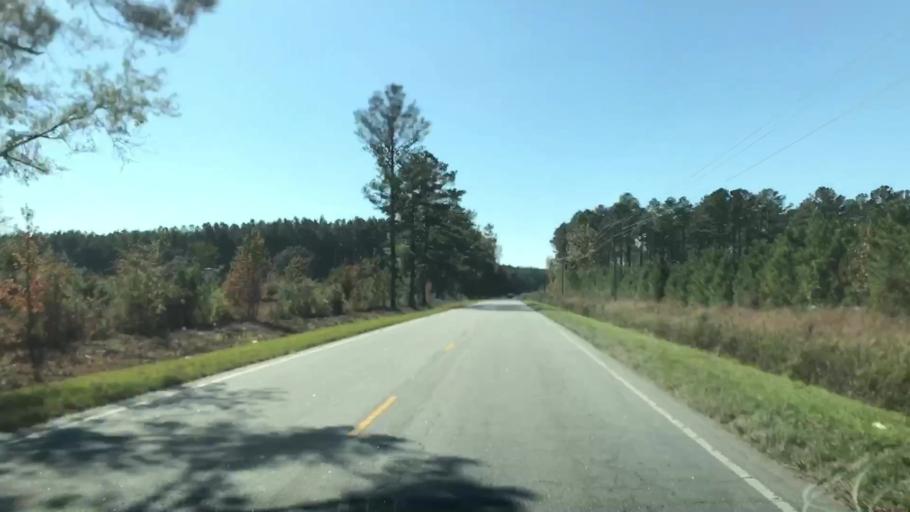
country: US
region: South Carolina
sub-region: Jasper County
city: Ridgeland
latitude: 32.4190
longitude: -80.8989
